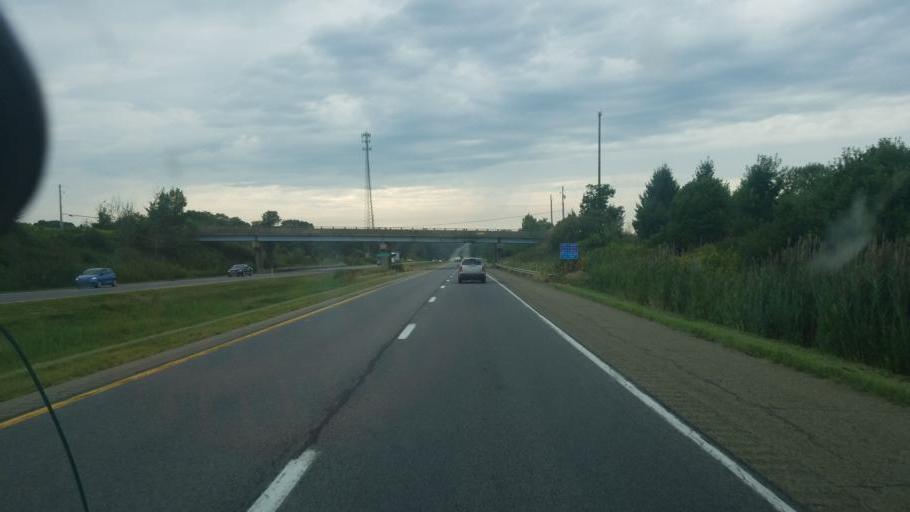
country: US
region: Pennsylvania
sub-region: Erie County
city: Girard
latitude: 41.9888
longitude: -80.2778
